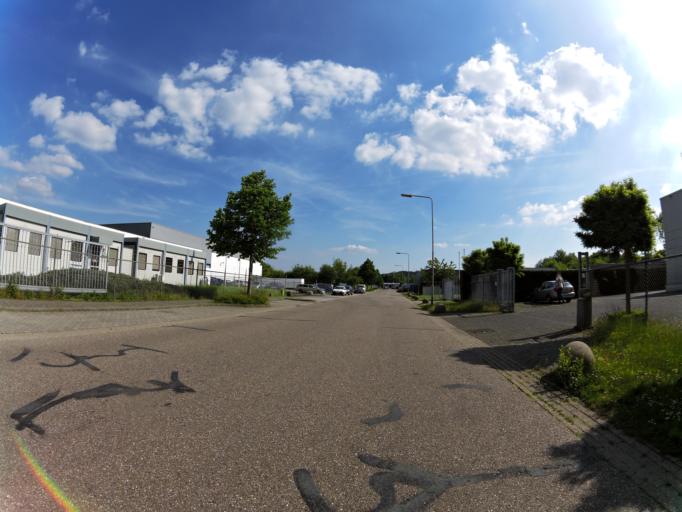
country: NL
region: Limburg
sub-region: Gemeente Heerlen
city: Heerlen
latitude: 50.8898
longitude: 6.0248
